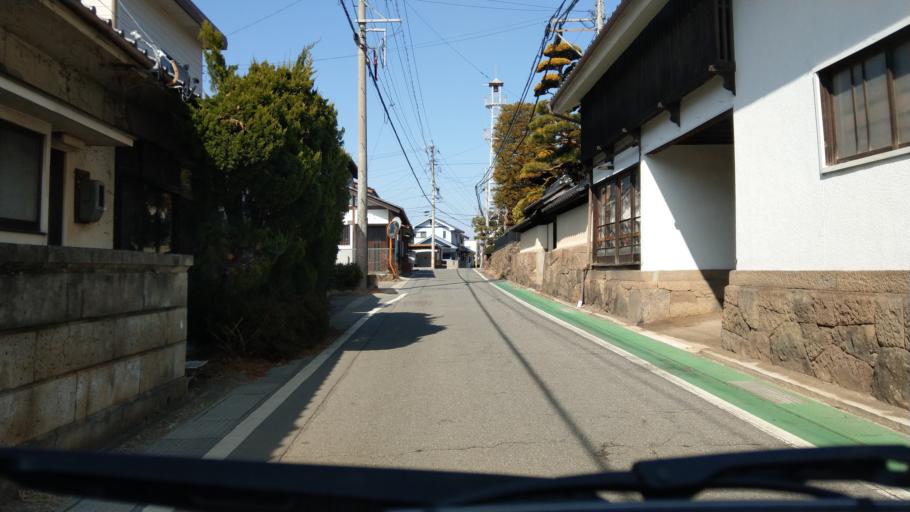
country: JP
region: Nagano
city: Ueda
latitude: 36.3738
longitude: 138.3523
